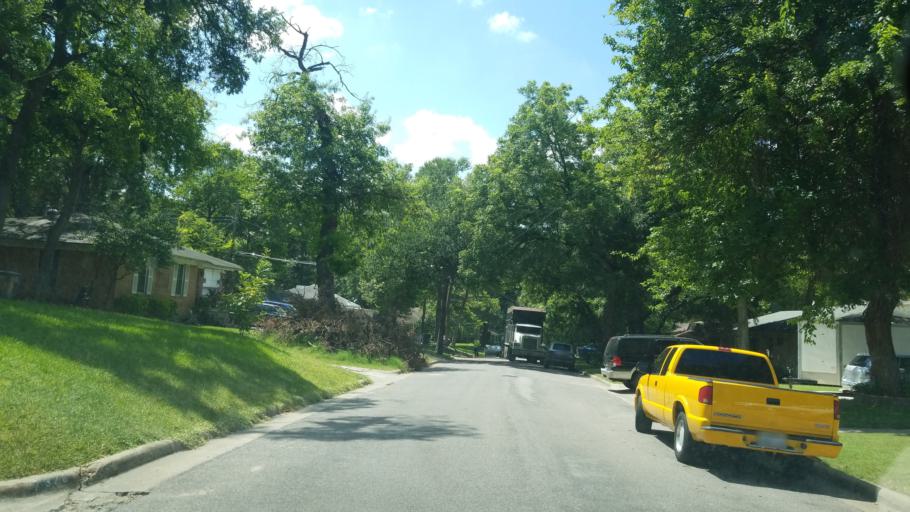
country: US
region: Texas
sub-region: Dallas County
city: Balch Springs
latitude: 32.7545
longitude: -96.6972
